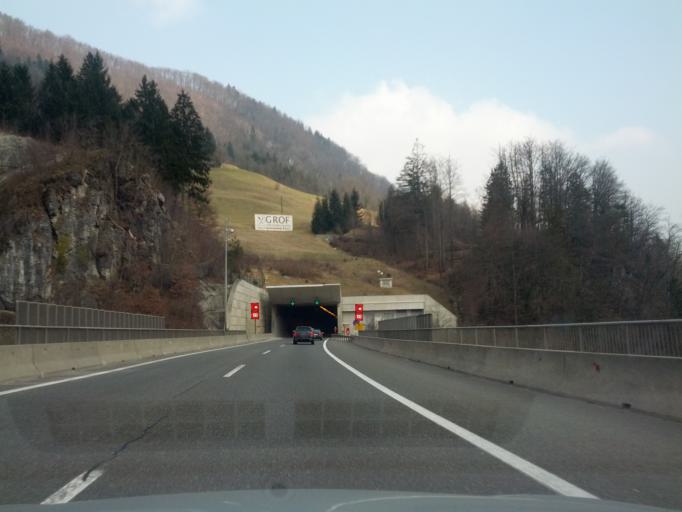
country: SI
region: Vransko
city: Vransko
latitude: 46.2063
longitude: 14.9017
